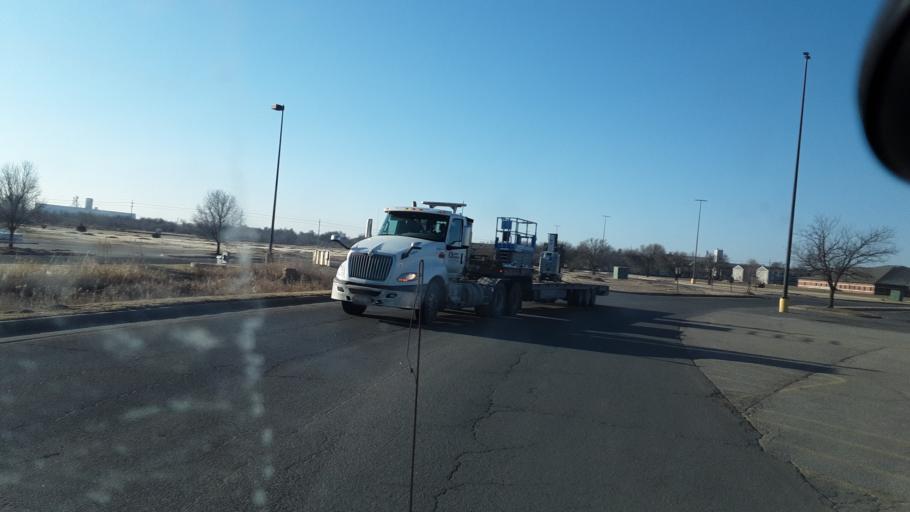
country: US
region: Kansas
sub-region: Reno County
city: Hutchinson
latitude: 38.0682
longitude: -97.8948
